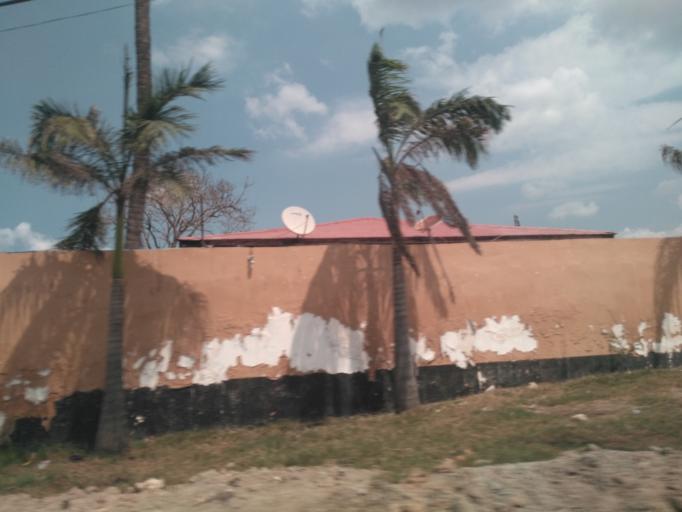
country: TZ
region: Dar es Salaam
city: Dar es Salaam
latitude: -6.8239
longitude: 39.3050
